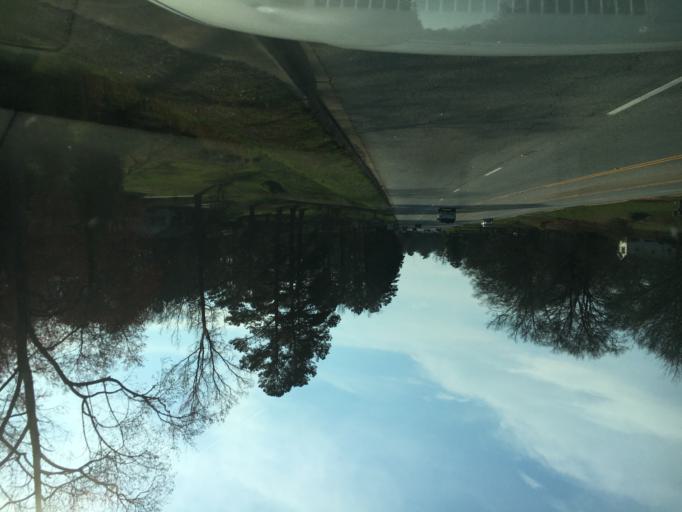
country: US
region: South Carolina
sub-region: Spartanburg County
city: Mayo
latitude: 35.0501
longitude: -81.8882
